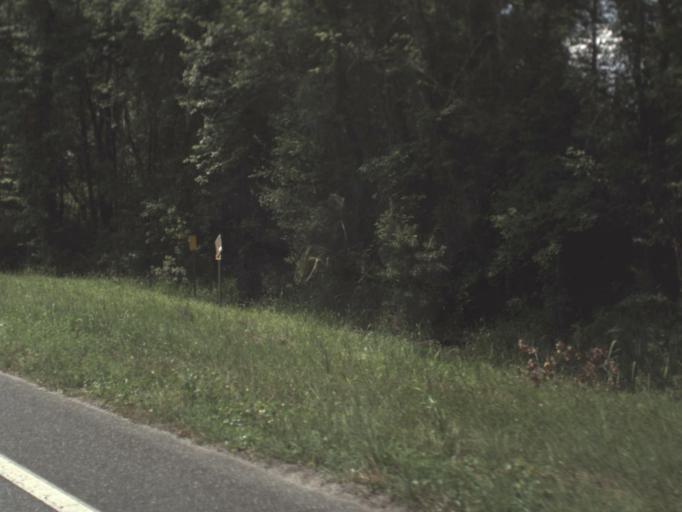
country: US
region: Georgia
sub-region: Echols County
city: Statenville
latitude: 30.5771
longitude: -83.0843
